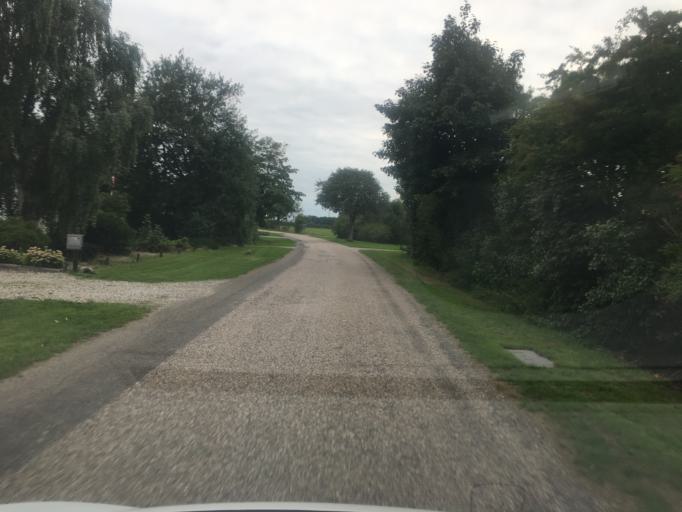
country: DK
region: South Denmark
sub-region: Tonder Kommune
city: Tonder
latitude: 54.9557
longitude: 8.9066
